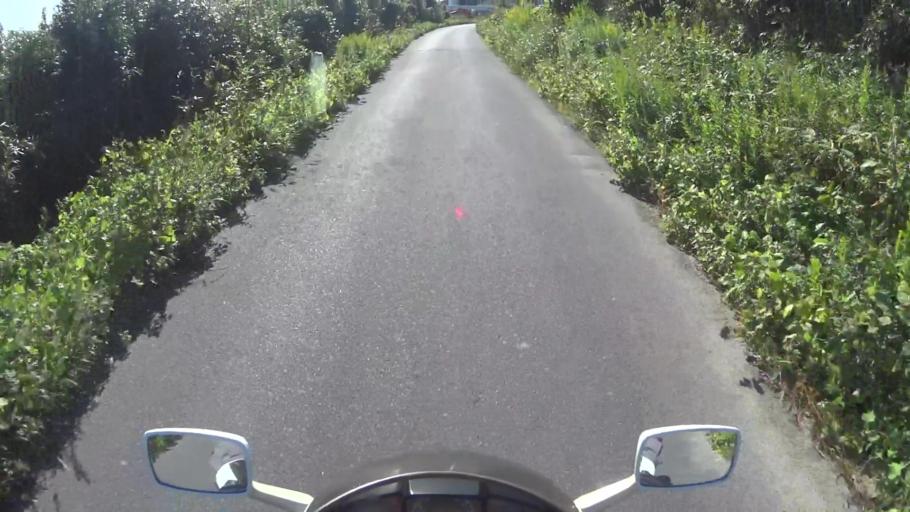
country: JP
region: Kyoto
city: Miyazu
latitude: 35.7473
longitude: 135.1069
